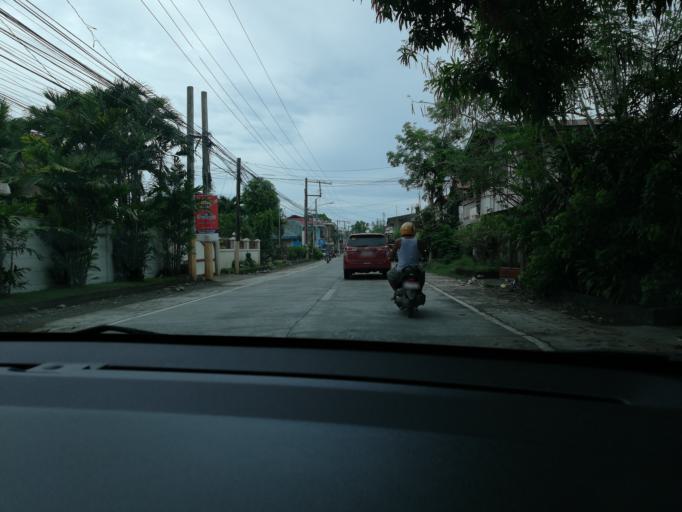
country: PH
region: Ilocos
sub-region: Province of Ilocos Sur
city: Bantay
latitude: 17.5823
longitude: 120.3869
